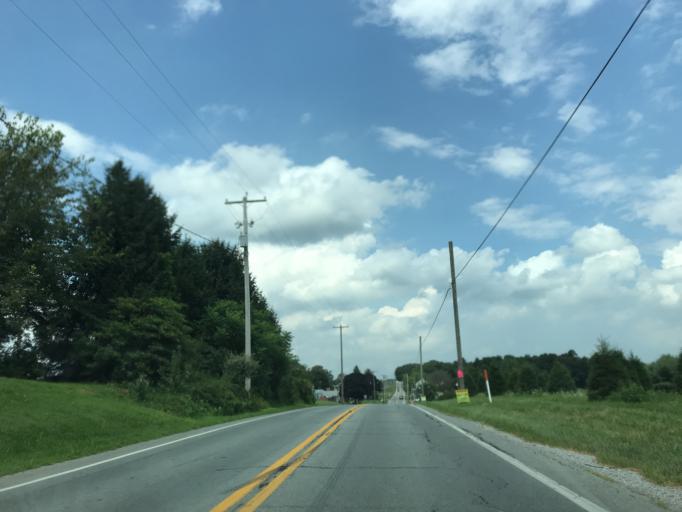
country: US
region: Pennsylvania
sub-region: York County
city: Red Lion
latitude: 39.8587
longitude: -76.6210
